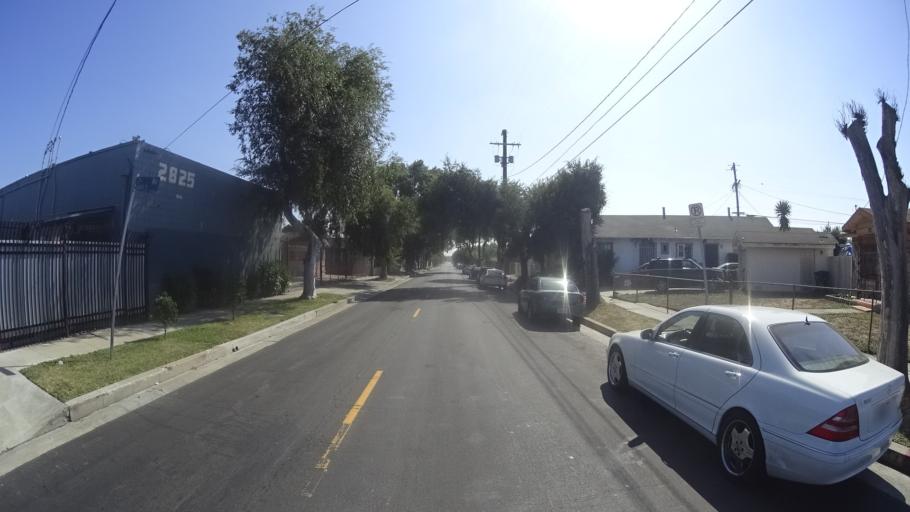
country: US
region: California
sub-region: Los Angeles County
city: View Park-Windsor Hills
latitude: 33.9801
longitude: -118.3245
